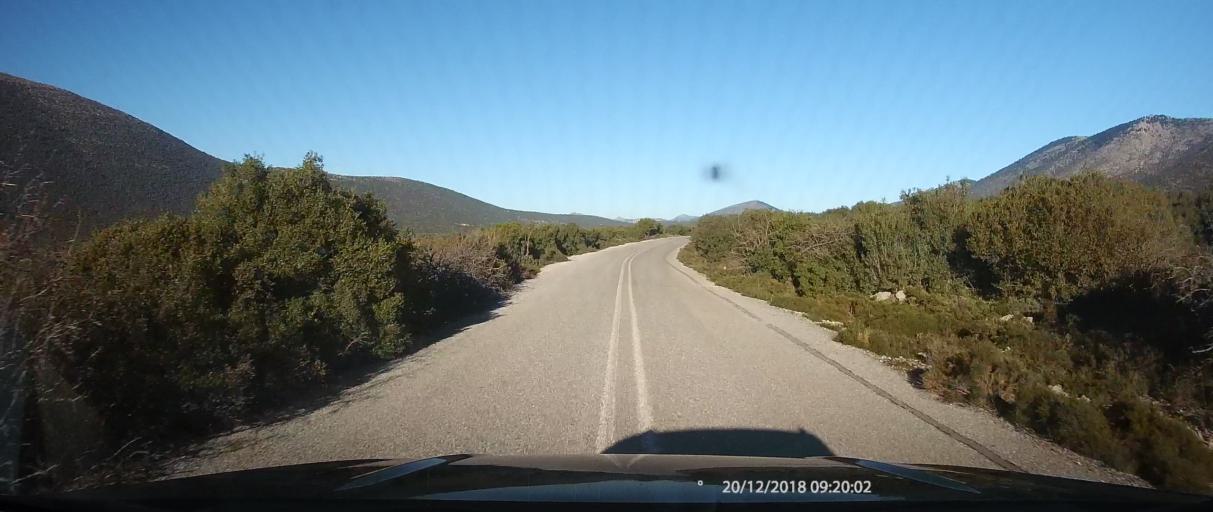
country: GR
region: Peloponnese
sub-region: Nomos Lakonias
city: Molaoi
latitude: 36.9239
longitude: 22.9300
